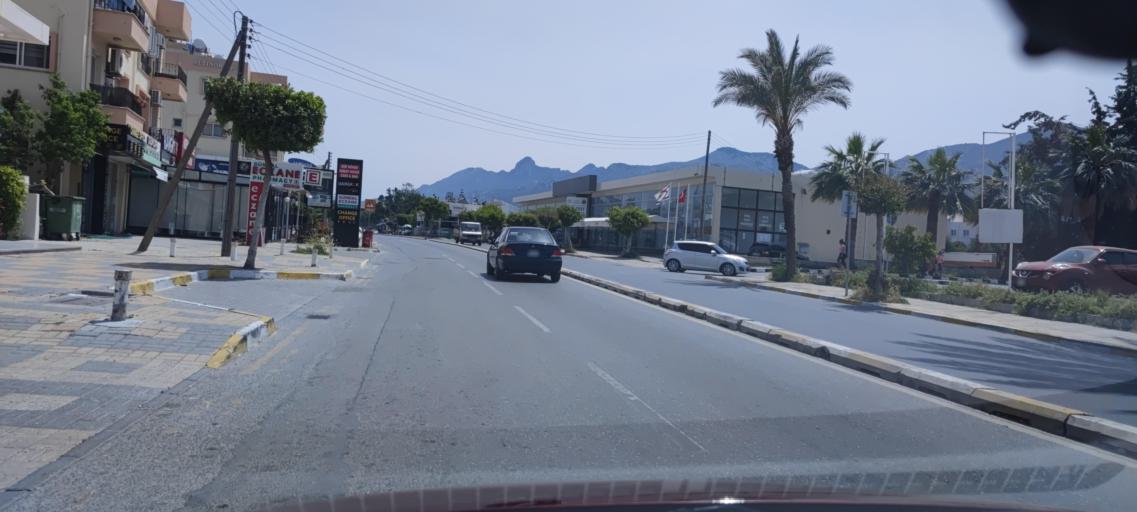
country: CY
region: Keryneia
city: Kyrenia
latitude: 35.3332
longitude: 33.3341
